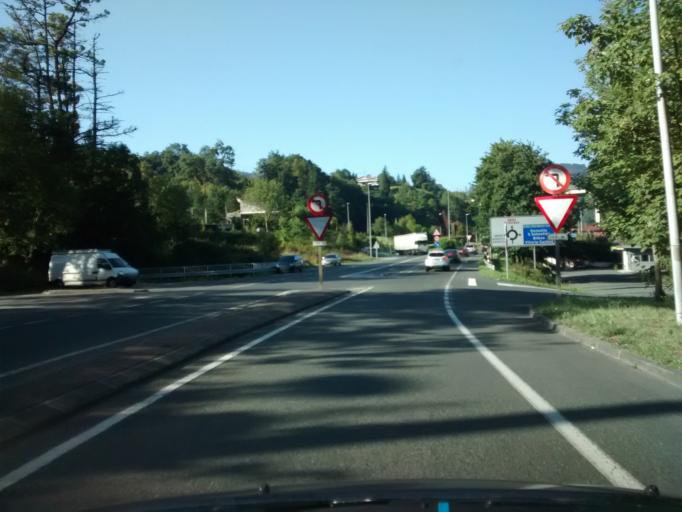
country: ES
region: Basque Country
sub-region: Provincia de Guipuzcoa
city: Elgoibar
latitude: 43.2297
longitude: -2.3996
